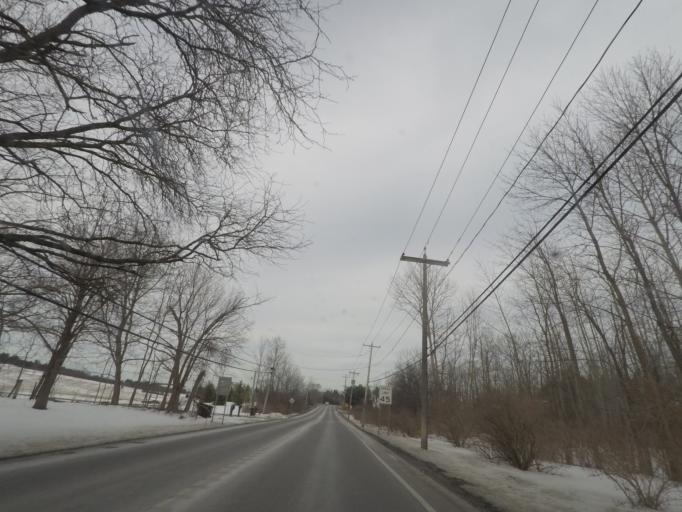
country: US
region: New York
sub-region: Albany County
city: Voorheesville
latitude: 42.5920
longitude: -73.9107
